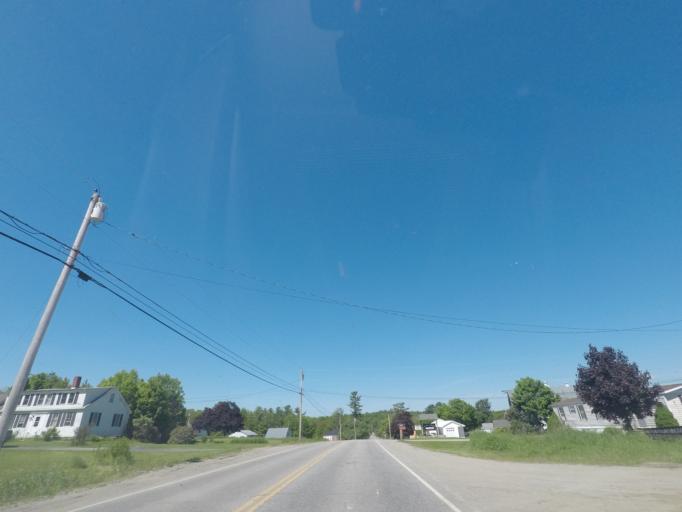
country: US
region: Maine
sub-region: Kennebec County
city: Gardiner
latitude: 44.2309
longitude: -69.8065
